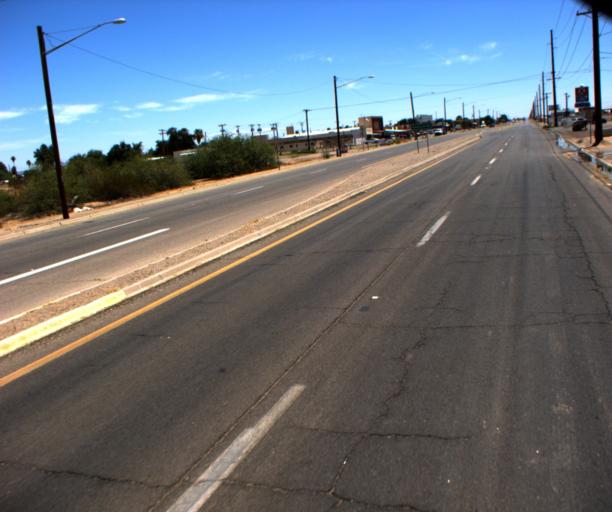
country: US
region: Arizona
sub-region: Pinal County
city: Maricopa
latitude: 32.8793
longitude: -111.9653
